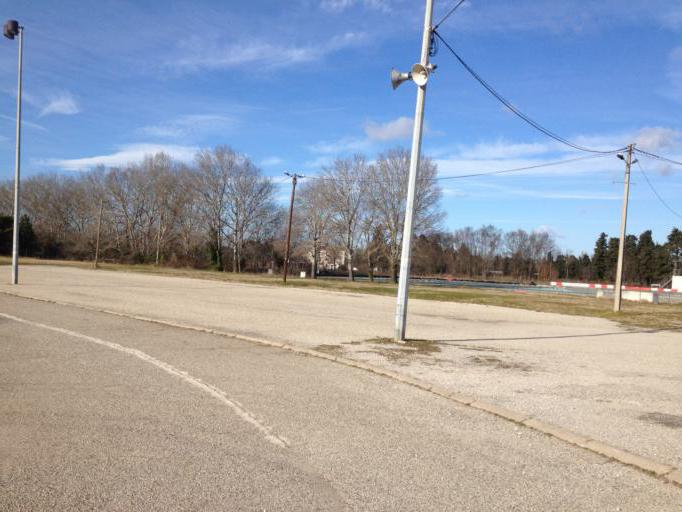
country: FR
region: Provence-Alpes-Cote d'Azur
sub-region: Departement du Vaucluse
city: Orange
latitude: 44.1294
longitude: 4.7965
